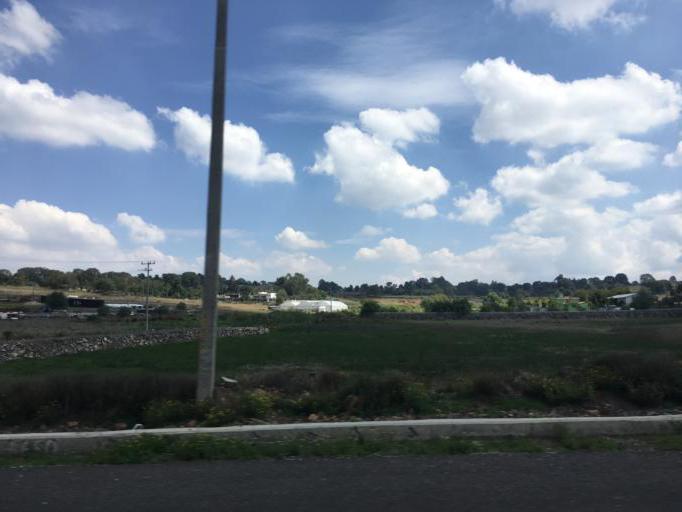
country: MX
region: Mexico
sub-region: Jilotepec
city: Octeyuco Dos Mil
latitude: 19.8893
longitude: -99.6372
